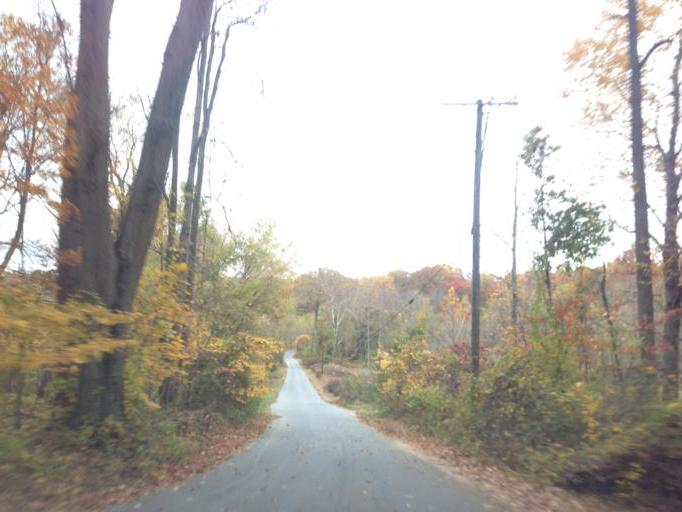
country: US
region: Maryland
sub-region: Baltimore County
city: Randallstown
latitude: 39.3790
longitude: -76.8557
